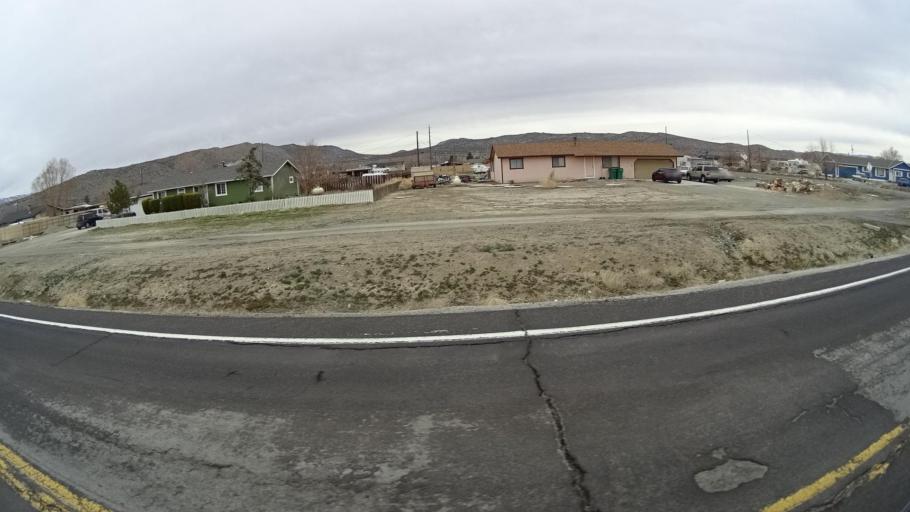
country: US
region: Nevada
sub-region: Washoe County
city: Lemmon Valley
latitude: 39.6729
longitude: -119.8390
